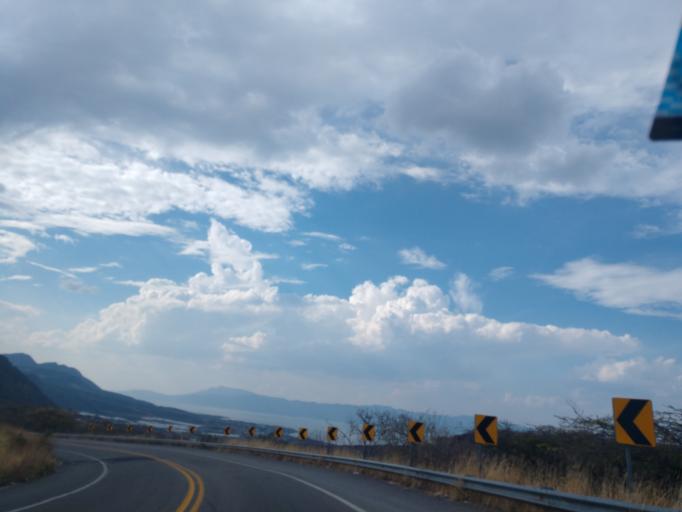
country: MX
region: Jalisco
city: Tizapan el Alto
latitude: 20.1244
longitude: -103.1552
